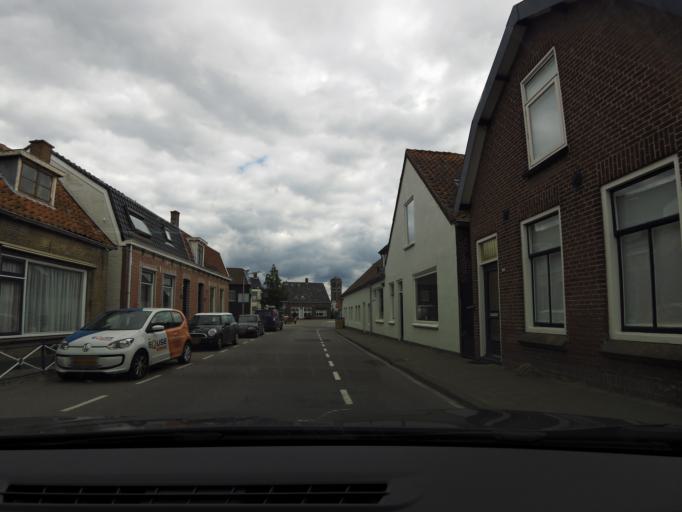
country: NL
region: South Holland
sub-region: Gemeente Binnenmaas
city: Mijnsheerenland
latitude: 51.7685
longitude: 4.4432
